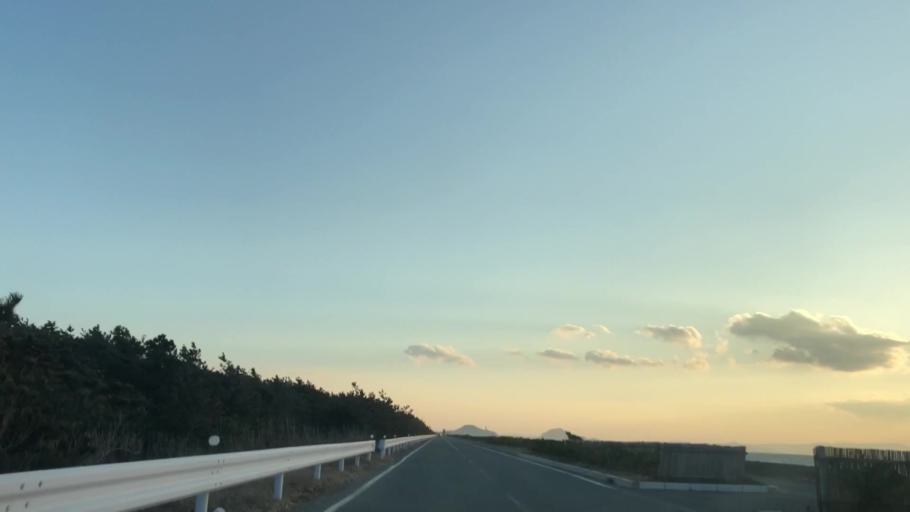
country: JP
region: Aichi
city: Toyohama
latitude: 34.6371
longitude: 137.0518
